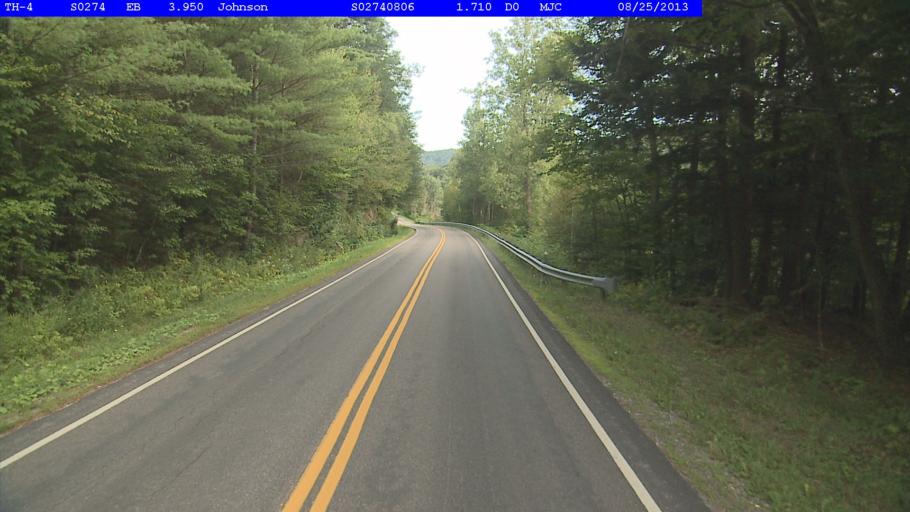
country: US
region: Vermont
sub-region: Lamoille County
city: Johnson
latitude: 44.6470
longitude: -72.7217
